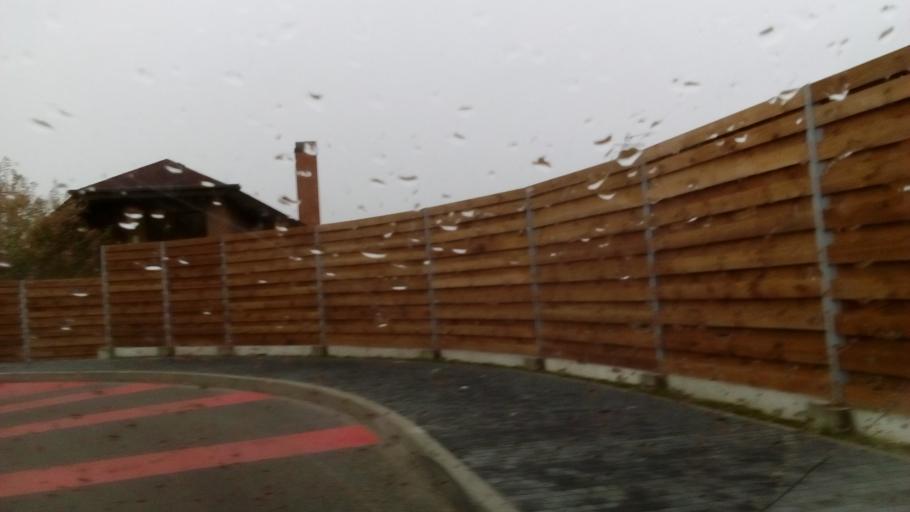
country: LT
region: Marijampoles apskritis
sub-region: Marijampole Municipality
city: Marijampole
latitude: 54.5447
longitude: 23.3552
